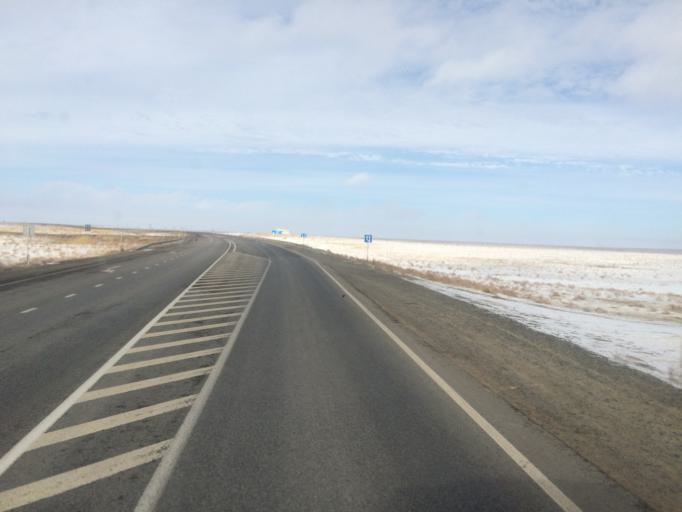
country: KZ
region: Qyzylorda
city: Aral
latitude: 46.8209
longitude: 61.7092
